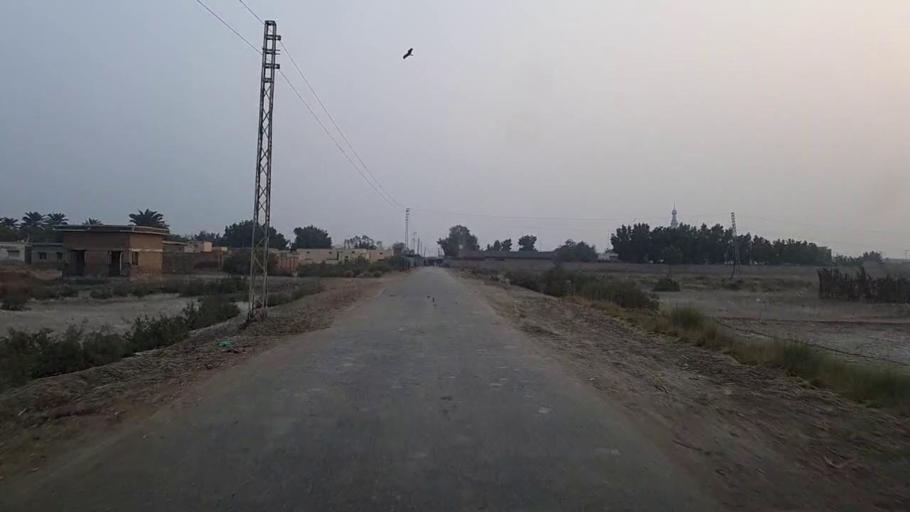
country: PK
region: Sindh
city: Kandiari
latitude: 26.9281
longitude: 68.5008
